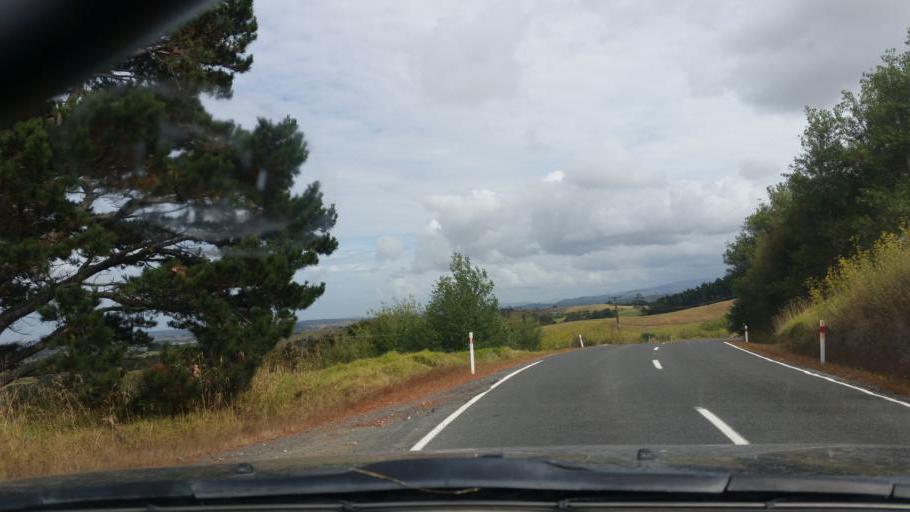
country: NZ
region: Northland
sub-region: Kaipara District
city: Dargaville
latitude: -35.9569
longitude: 173.9233
